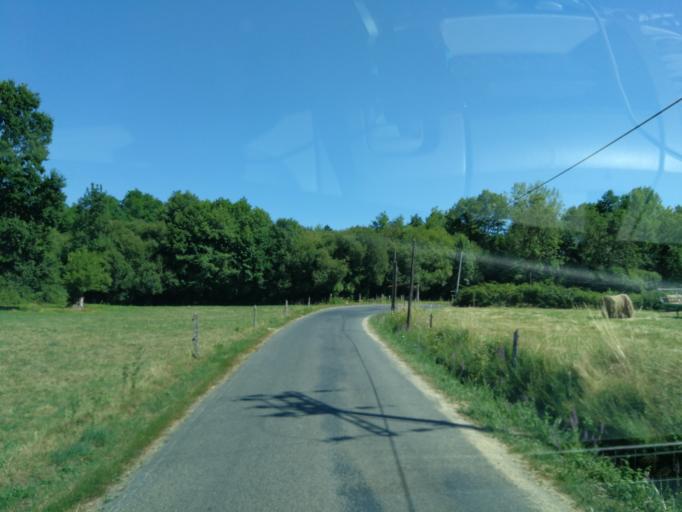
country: FR
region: Limousin
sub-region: Departement de la Correze
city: Sainte-Fereole
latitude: 45.2364
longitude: 1.5938
